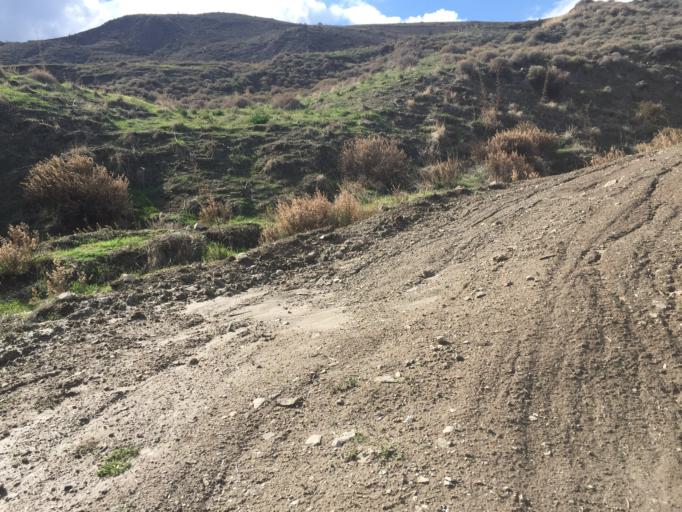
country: CY
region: Limassol
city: Pachna
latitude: 34.8719
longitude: 32.6598
